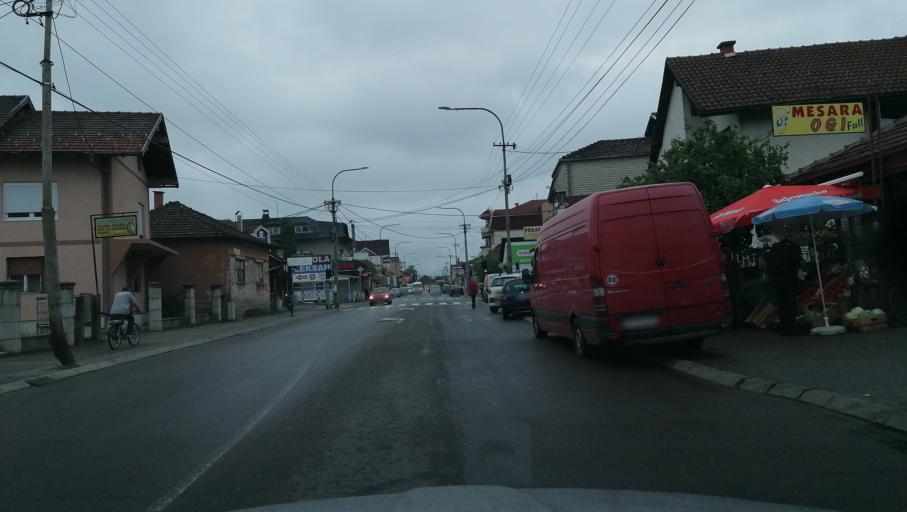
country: RS
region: Central Serbia
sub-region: Rasinski Okrug
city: Krusevac
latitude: 43.5835
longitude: 21.3127
